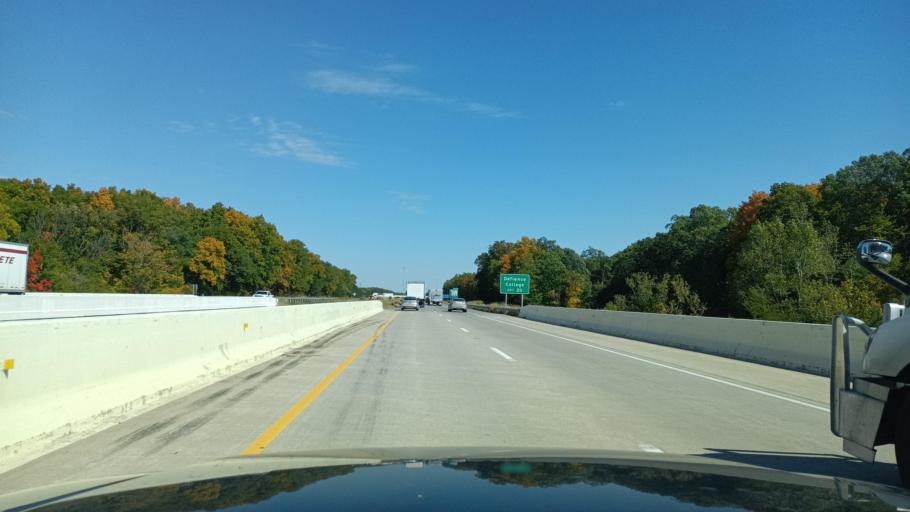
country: US
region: Ohio
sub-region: Defiance County
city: Defiance
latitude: 41.2957
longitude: -84.3859
